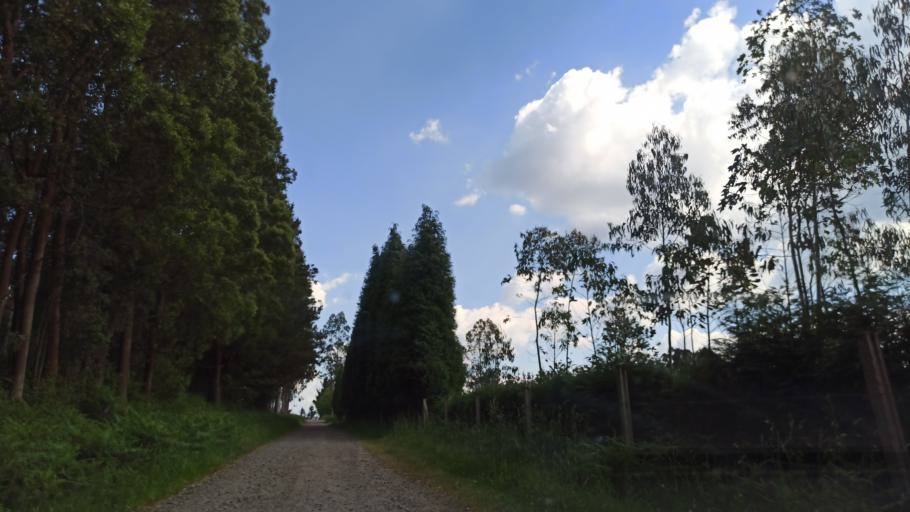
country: ES
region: Galicia
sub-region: Provincia da Coruna
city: Santa Comba
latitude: 43.0770
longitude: -8.7175
